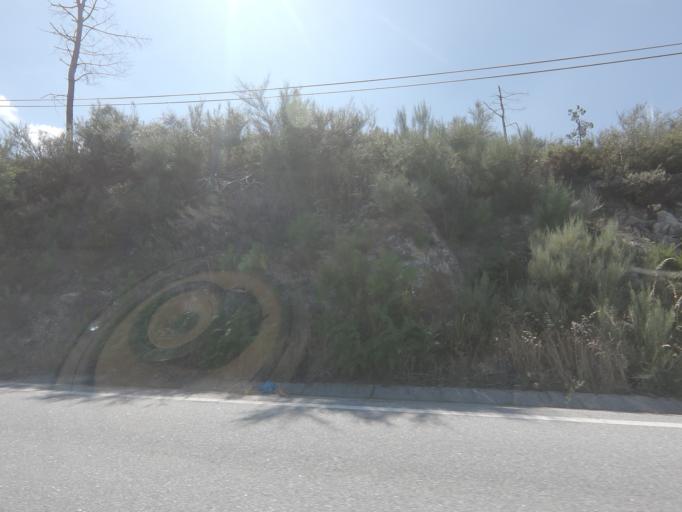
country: PT
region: Viseu
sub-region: Tarouca
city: Tarouca
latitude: 41.0001
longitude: -7.7812
